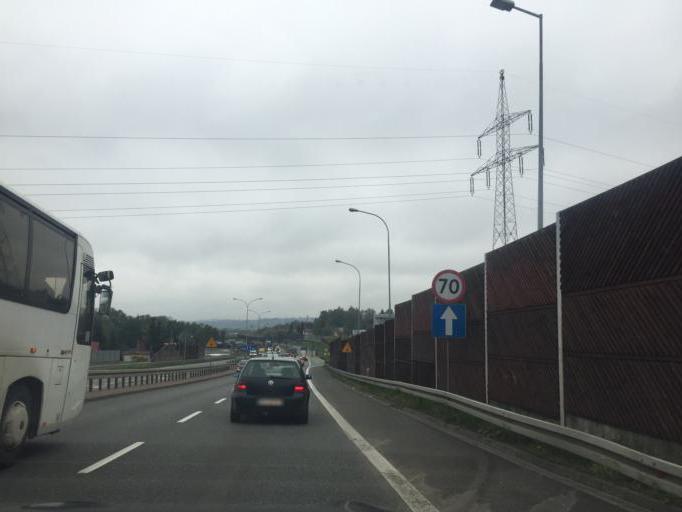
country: PL
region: Lesser Poland Voivodeship
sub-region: Powiat wielicki
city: Wieliczka
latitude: 50.0013
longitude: 20.0260
